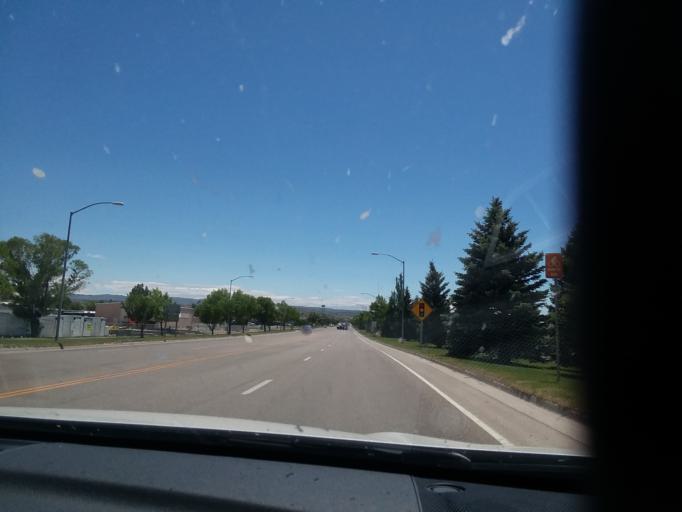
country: US
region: Wyoming
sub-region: Sweetwater County
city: North Rock Springs
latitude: 41.6205
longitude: -109.2330
